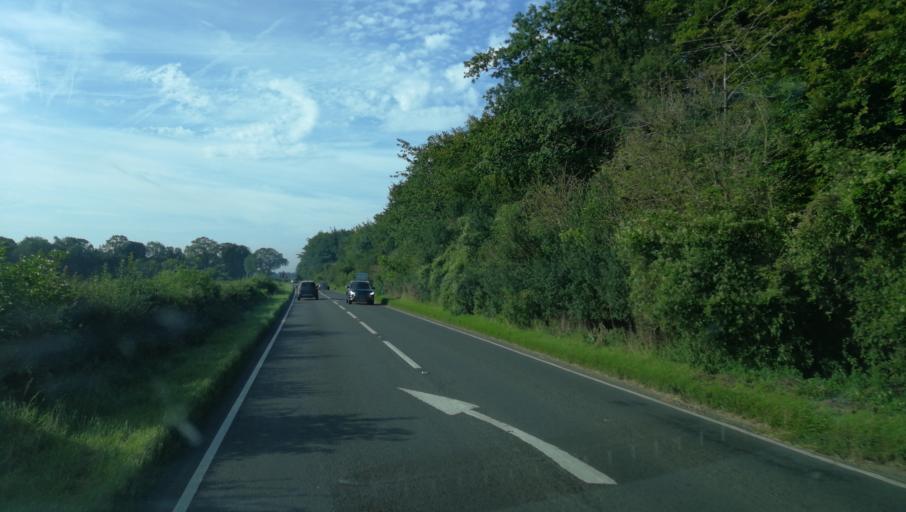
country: GB
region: England
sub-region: Oxfordshire
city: Woodstock
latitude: 51.9018
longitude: -1.3289
